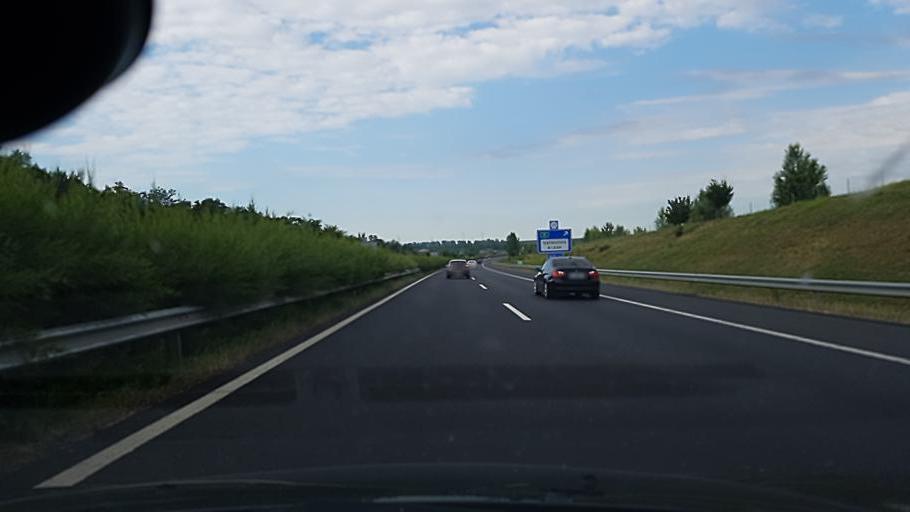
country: HU
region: Pest
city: Szazhalombatta
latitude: 47.3480
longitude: 18.9010
